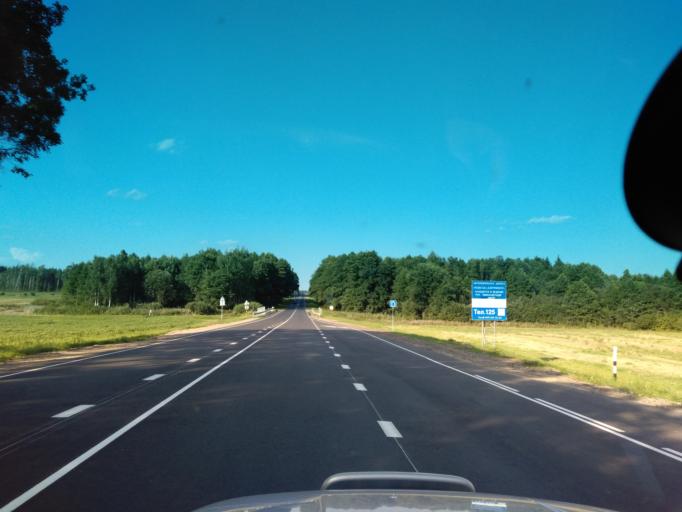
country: BY
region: Minsk
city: Dzyarzhynsk
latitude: 53.6571
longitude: 27.0793
